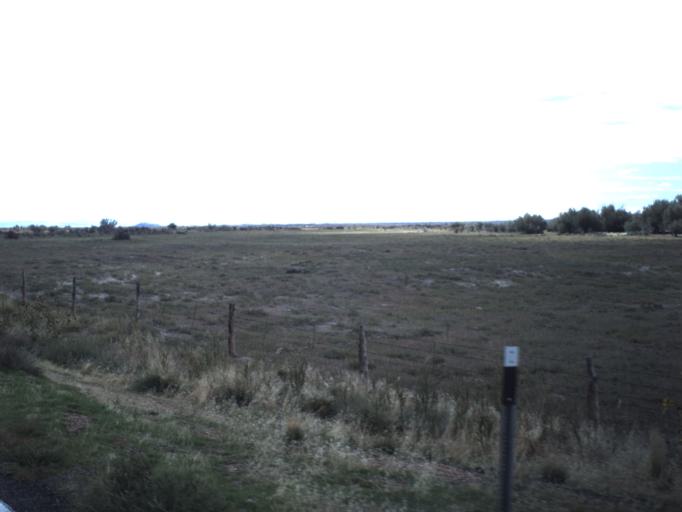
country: US
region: Utah
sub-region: Millard County
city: Fillmore
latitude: 39.1079
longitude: -112.4098
